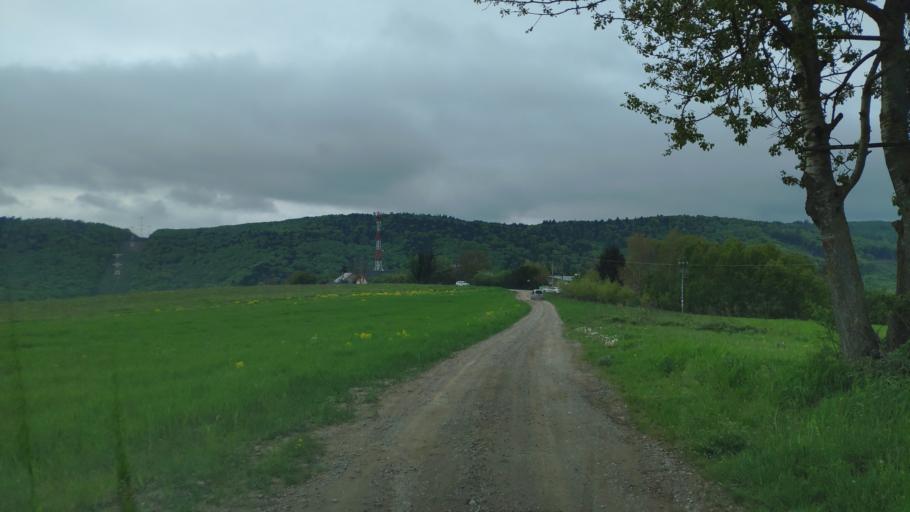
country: SK
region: Kosicky
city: Kosice
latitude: 48.7611
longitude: 21.2017
